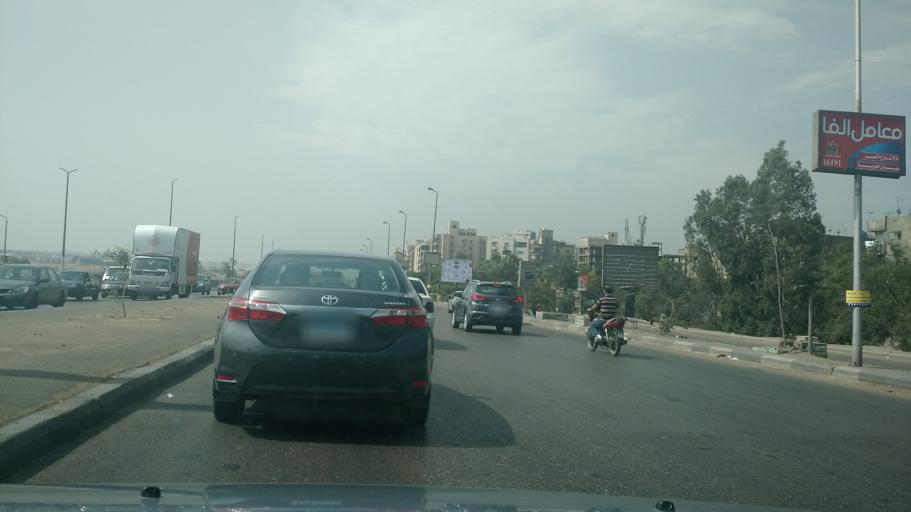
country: EG
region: Al Jizah
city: Al Jizah
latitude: 29.9804
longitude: 31.2894
